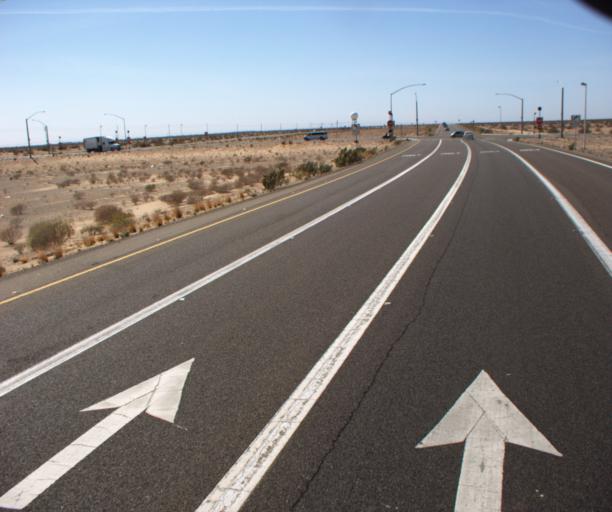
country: US
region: Arizona
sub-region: Yuma County
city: Somerton
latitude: 32.4969
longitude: -114.6466
